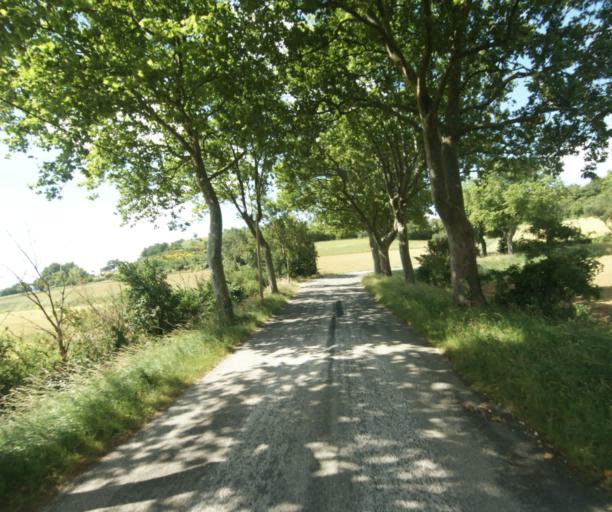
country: FR
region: Midi-Pyrenees
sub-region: Departement de la Haute-Garonne
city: Saint-Felix-Lauragais
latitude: 43.4488
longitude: 1.9019
